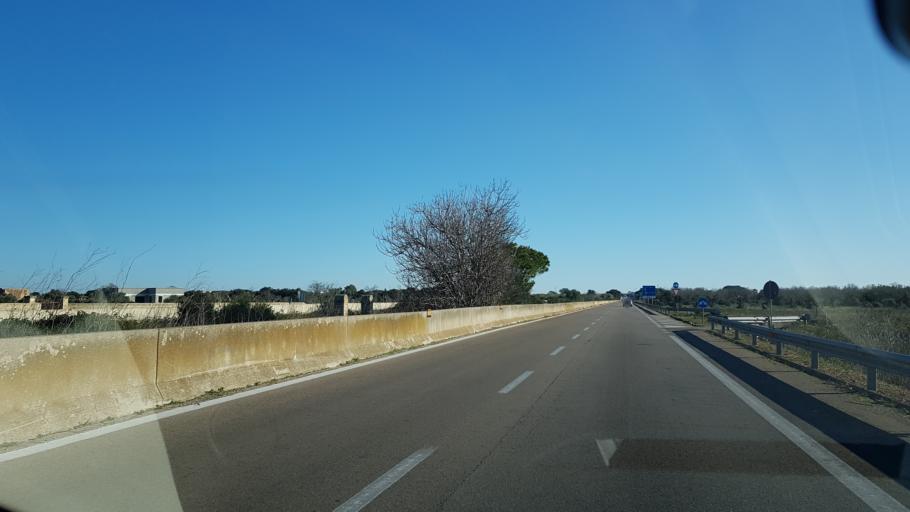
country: IT
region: Apulia
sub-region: Provincia di Lecce
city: Alezio
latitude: 40.0216
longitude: 18.0407
